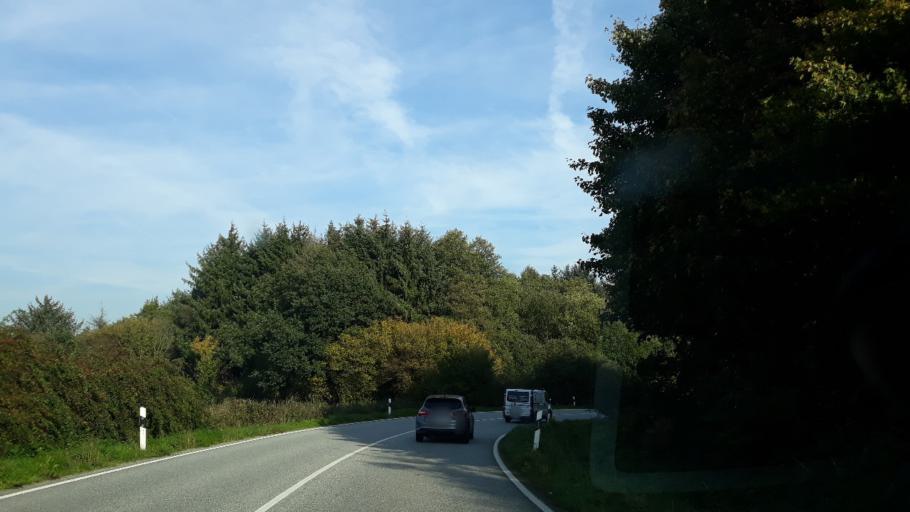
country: DE
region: Schleswig-Holstein
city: Schleswig
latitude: 54.5374
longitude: 9.5579
